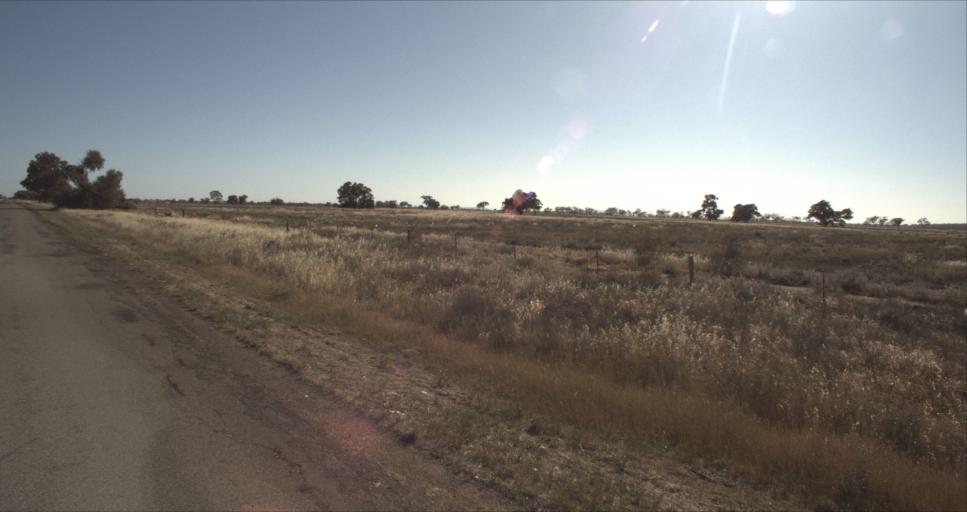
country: AU
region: New South Wales
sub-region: Leeton
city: Leeton
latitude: -34.6009
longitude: 146.2577
